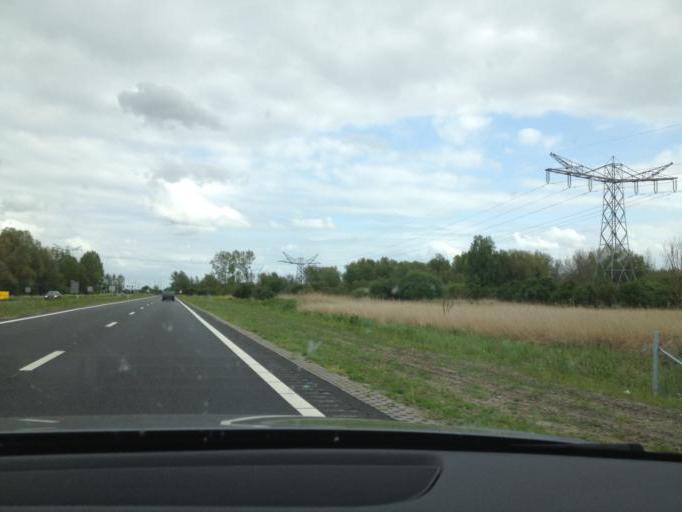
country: NL
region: Utrecht
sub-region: Gemeente Bunschoten
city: Spakenburg
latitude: 52.3114
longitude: 5.3395
